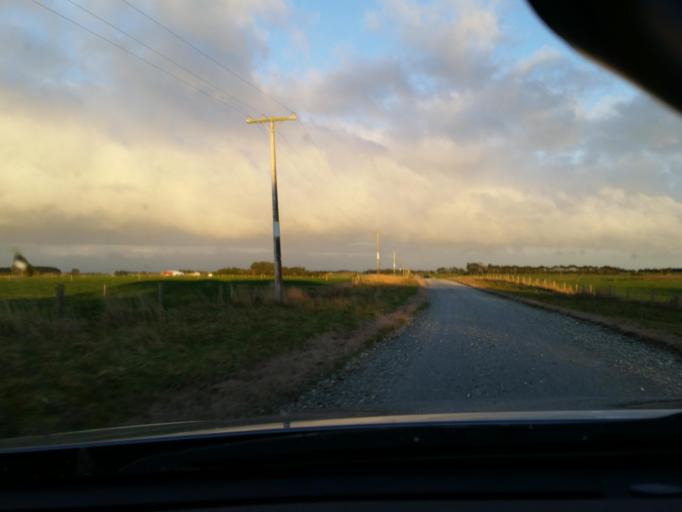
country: NZ
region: Southland
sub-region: Invercargill City
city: Invercargill
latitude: -46.4097
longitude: 168.7085
